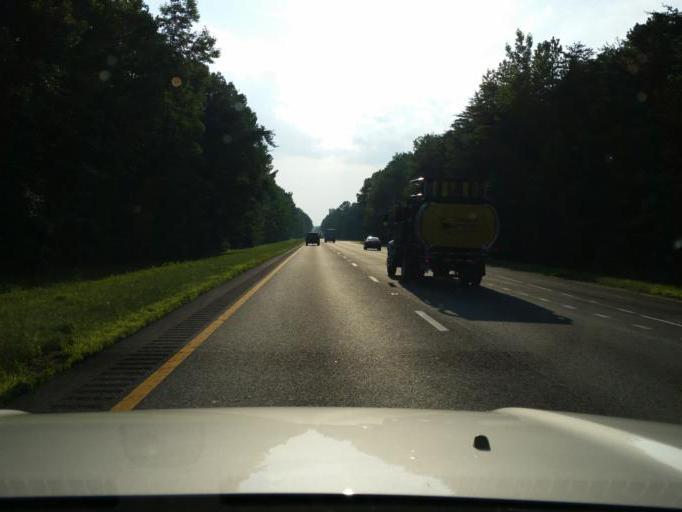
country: US
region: Virginia
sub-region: New Kent County
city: New Kent
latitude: 37.4947
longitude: -77.0162
